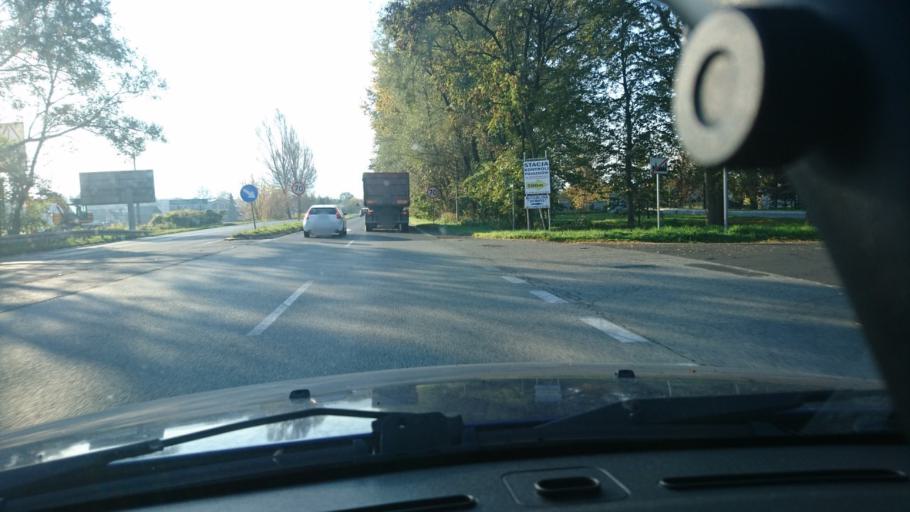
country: PL
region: Silesian Voivodeship
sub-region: Powiat cieszynski
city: Gorki Wielkie
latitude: 49.7815
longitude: 18.8066
